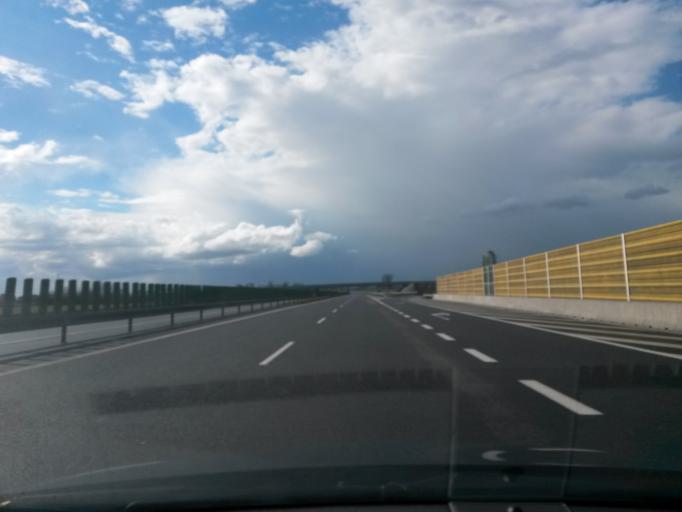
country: PL
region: Greater Poland Voivodeship
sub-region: Powiat wrzesinski
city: Wrzesnia
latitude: 52.3144
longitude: 17.5386
